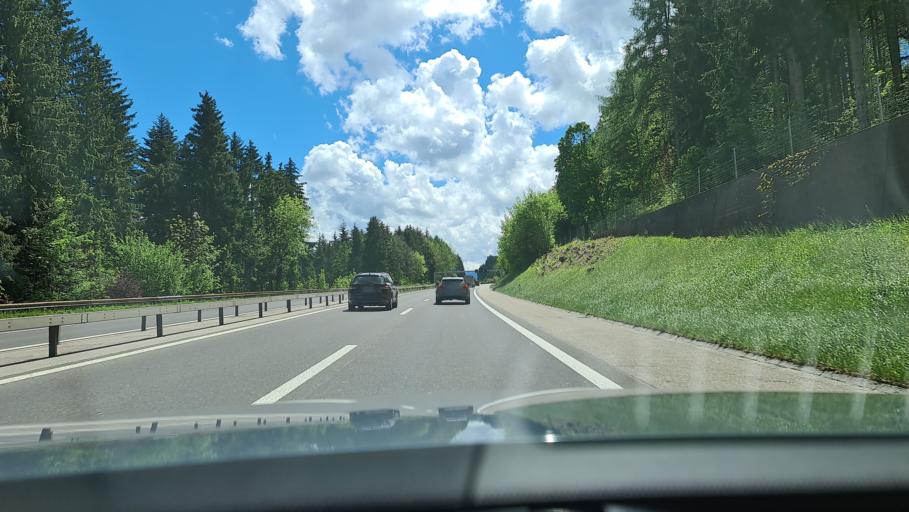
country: CH
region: Zurich
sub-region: Bezirk Horgen
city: Thalwil / Berg
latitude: 47.2833
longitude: 8.5588
